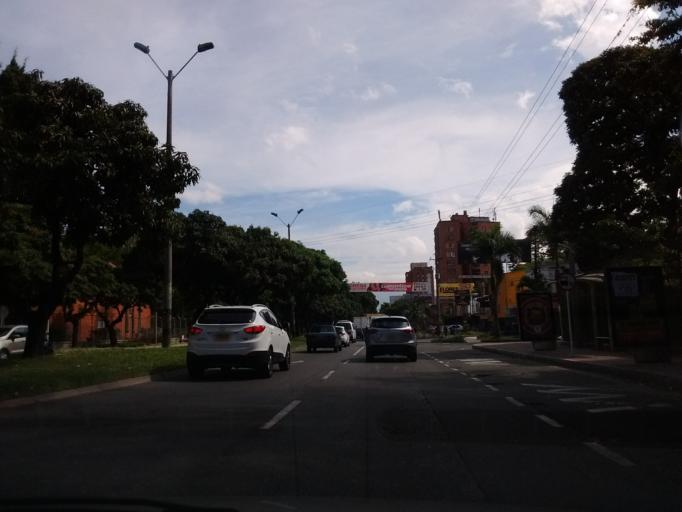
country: CO
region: Antioquia
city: Itagui
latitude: 6.2072
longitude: -75.5768
